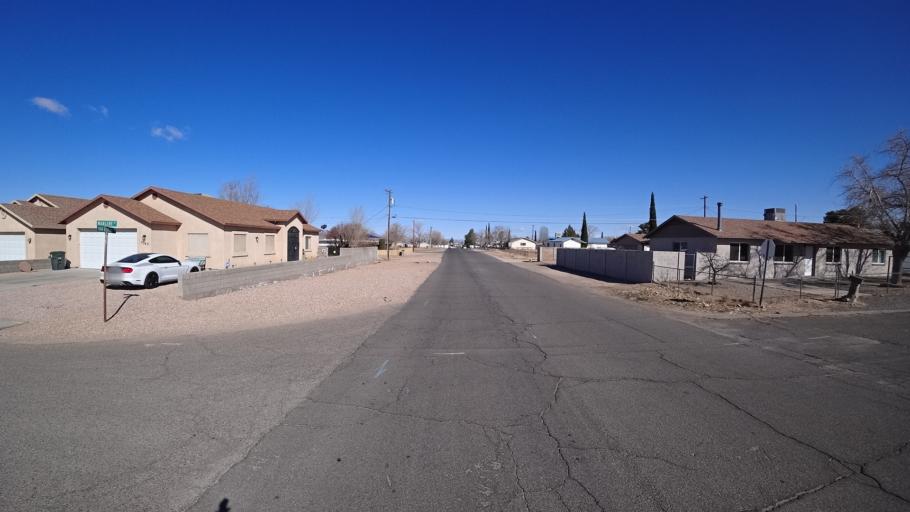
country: US
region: Arizona
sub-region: Mohave County
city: Kingman
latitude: 35.1931
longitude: -114.0224
